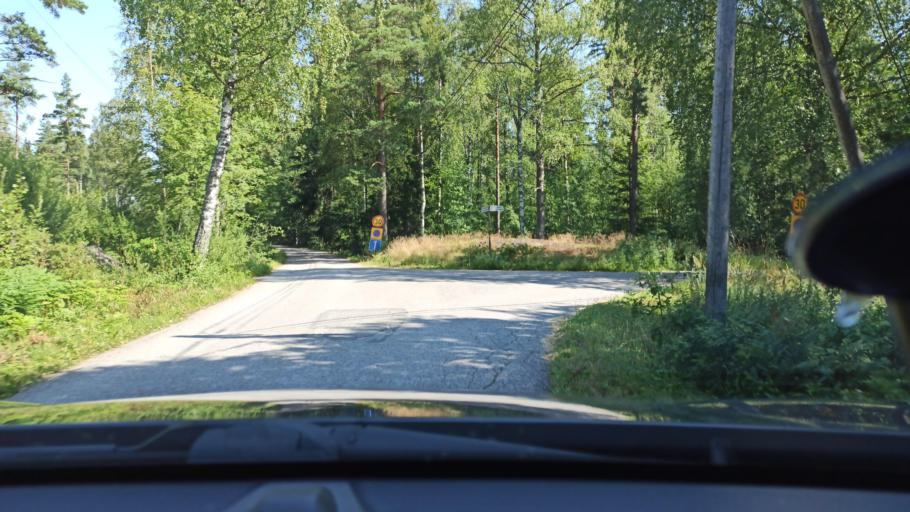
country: FI
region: Uusimaa
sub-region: Helsinki
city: Espoo
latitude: 60.1530
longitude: 24.5680
